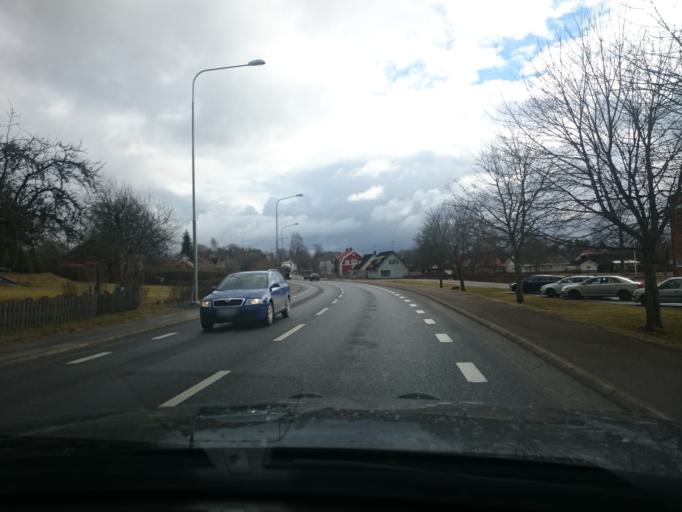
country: SE
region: Joenkoeping
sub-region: Vetlanda Kommun
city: Vetlanda
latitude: 57.3050
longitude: 15.1247
